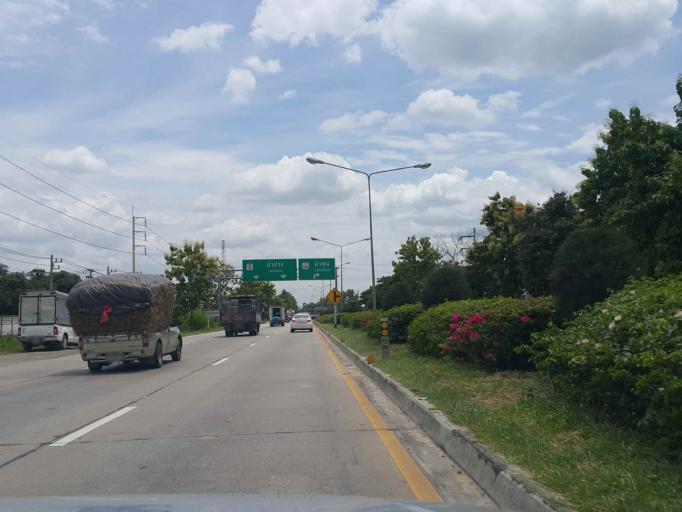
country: TH
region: Lamphun
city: Lamphun
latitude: 18.6174
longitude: 99.0461
